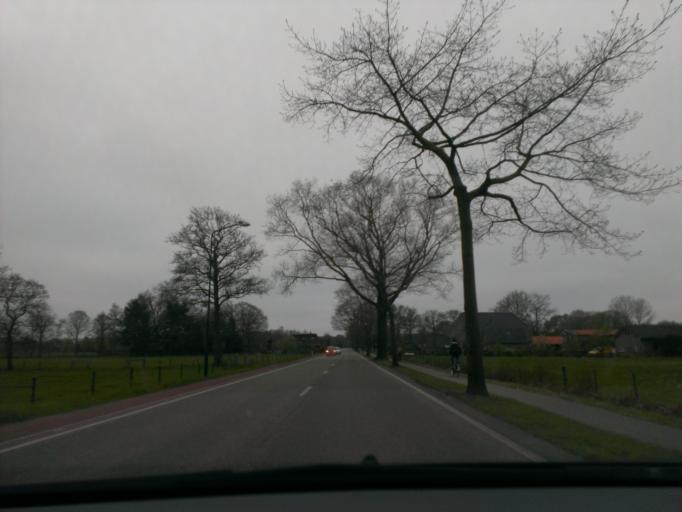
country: NL
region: Gelderland
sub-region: Gemeente Epe
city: Vaassen
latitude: 52.2673
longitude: 5.9569
